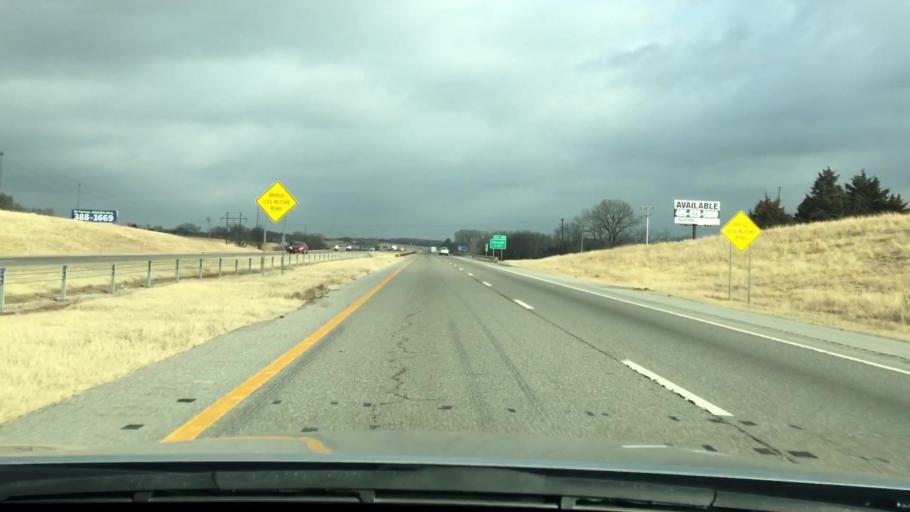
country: US
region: Oklahoma
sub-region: McClain County
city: Purcell
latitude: 35.0273
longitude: -97.3758
